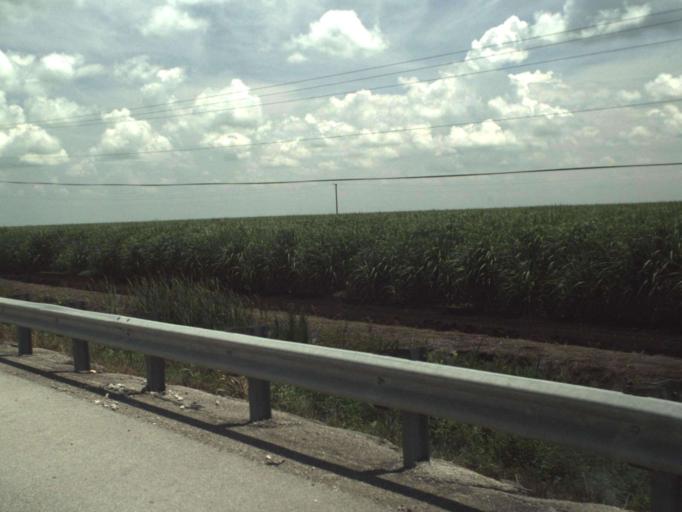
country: US
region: Florida
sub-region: Palm Beach County
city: Pahokee
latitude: 26.8438
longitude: -80.6043
